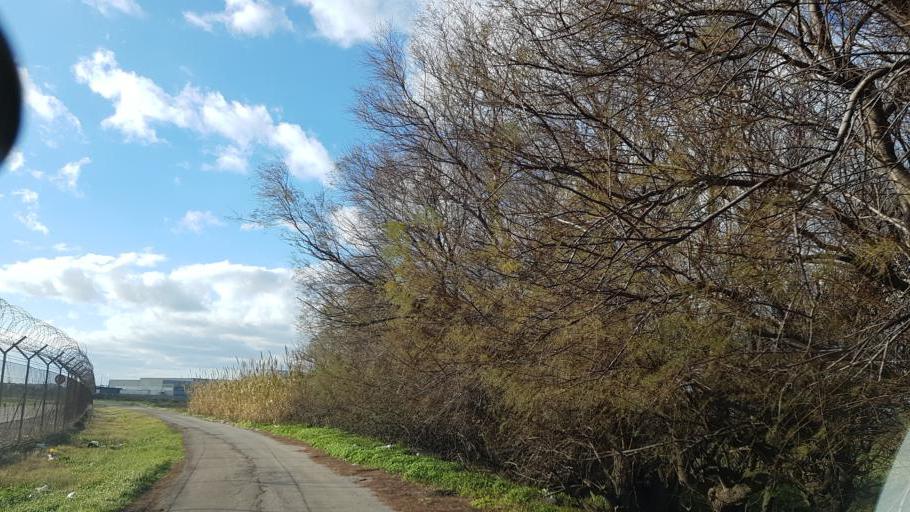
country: IT
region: Apulia
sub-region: Provincia di Brindisi
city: Materdomini
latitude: 40.6777
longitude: 17.9227
